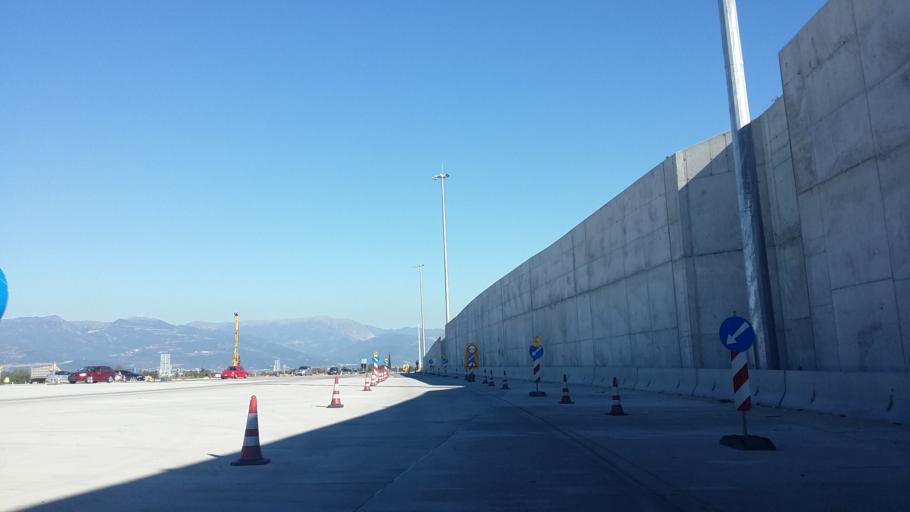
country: GR
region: West Greece
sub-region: Nomos Achaias
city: Ano Kastritsion
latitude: 38.3165
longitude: 21.8307
